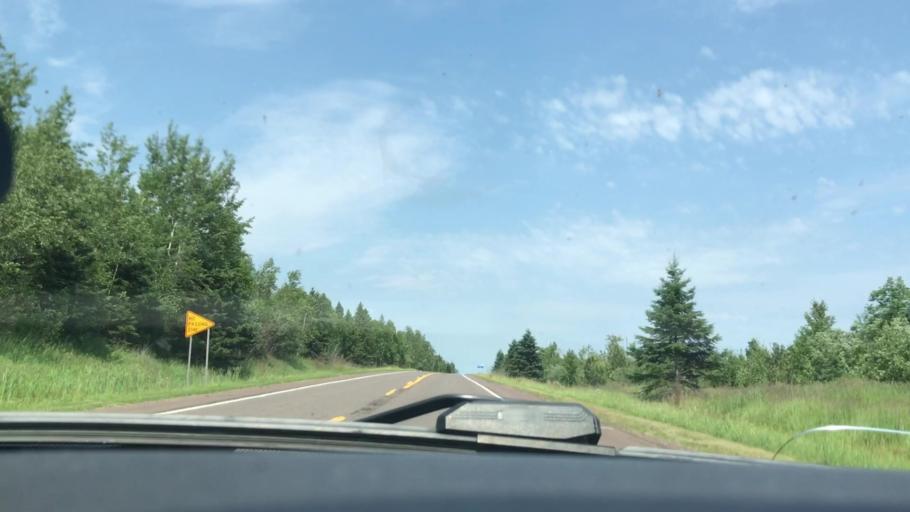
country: US
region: Minnesota
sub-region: Lake County
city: Silver Bay
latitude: 47.4459
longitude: -91.0665
